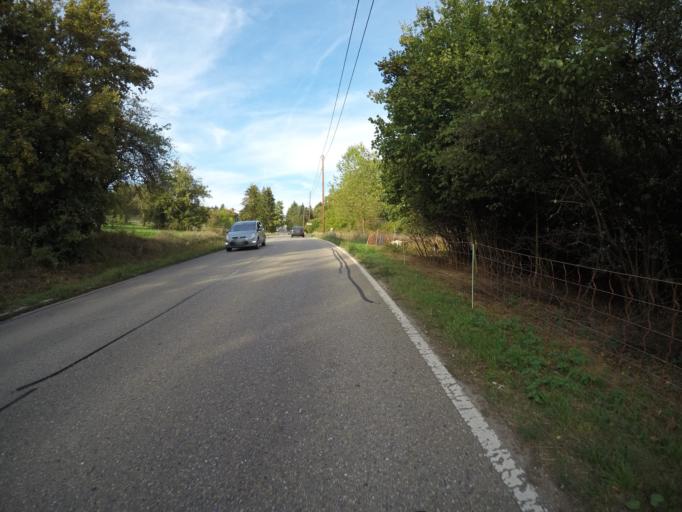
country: DE
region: Baden-Wuerttemberg
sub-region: Regierungsbezirk Stuttgart
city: Neuhausen auf den Fildern
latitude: 48.7045
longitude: 9.2886
